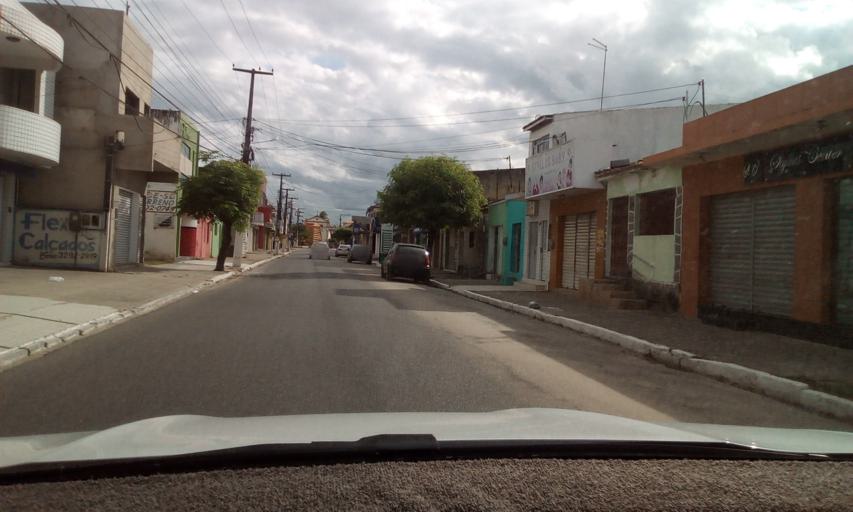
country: BR
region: Paraiba
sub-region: Mamanguape
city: Mamanguape
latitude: -6.8377
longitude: -35.1308
